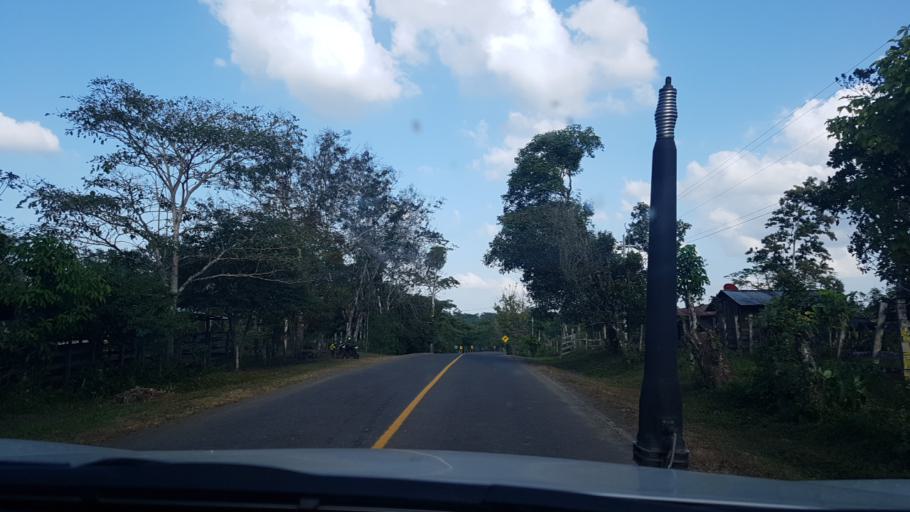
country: NI
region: Atlantico Sur
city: Nueva Guinea
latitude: 11.6958
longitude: -84.4097
